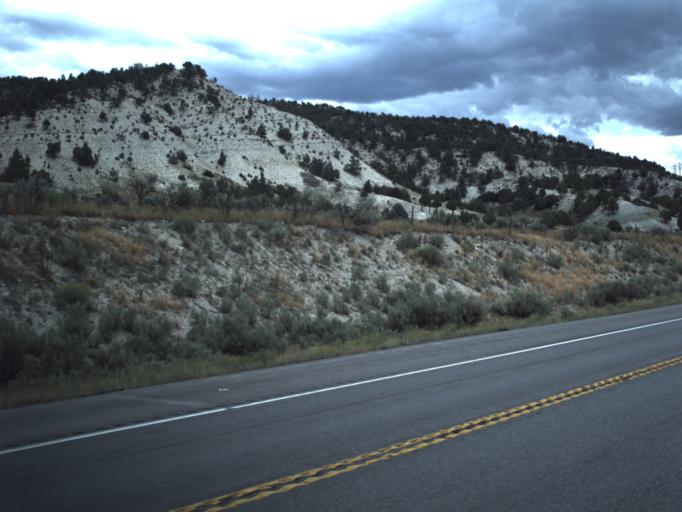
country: US
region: Utah
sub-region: Utah County
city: Mapleton
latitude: 39.9695
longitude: -111.3282
